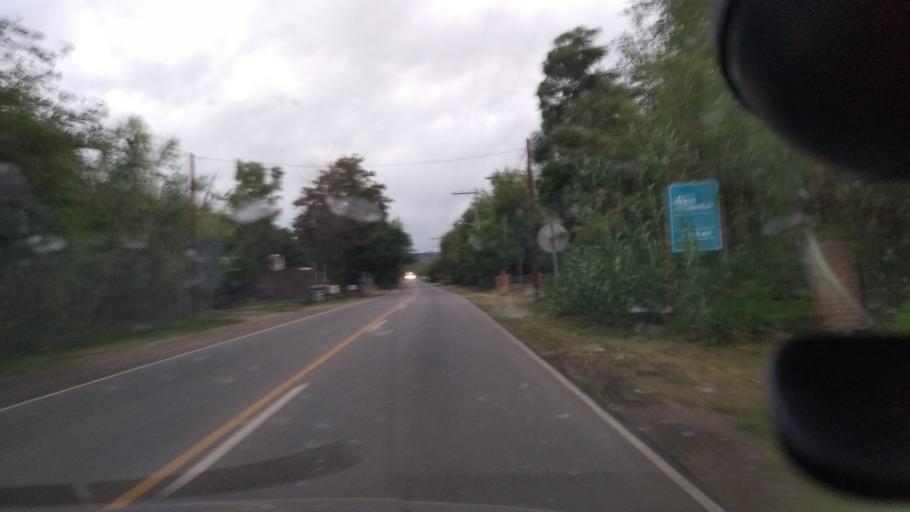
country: AR
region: Cordoba
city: Villa Las Rosas
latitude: -31.9355
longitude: -65.0409
